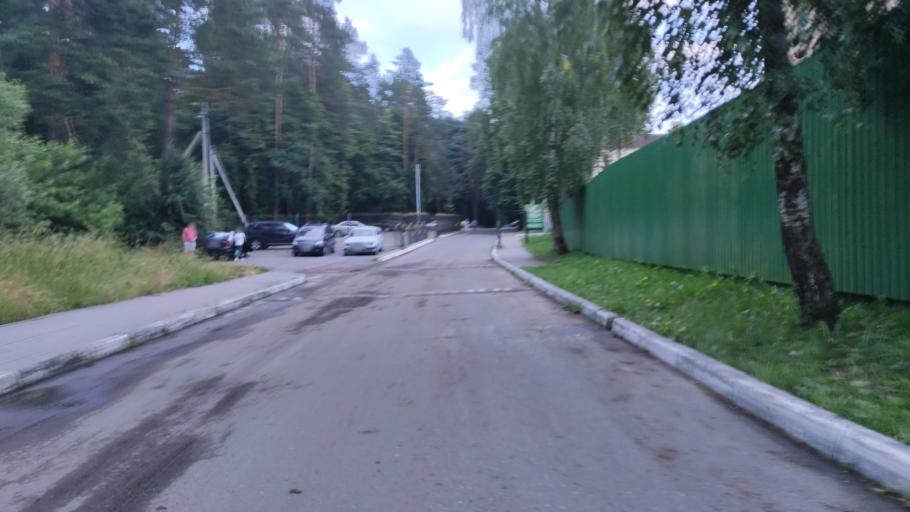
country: BY
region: Minsk
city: Zhdanovichy
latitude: 53.9682
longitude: 27.4310
